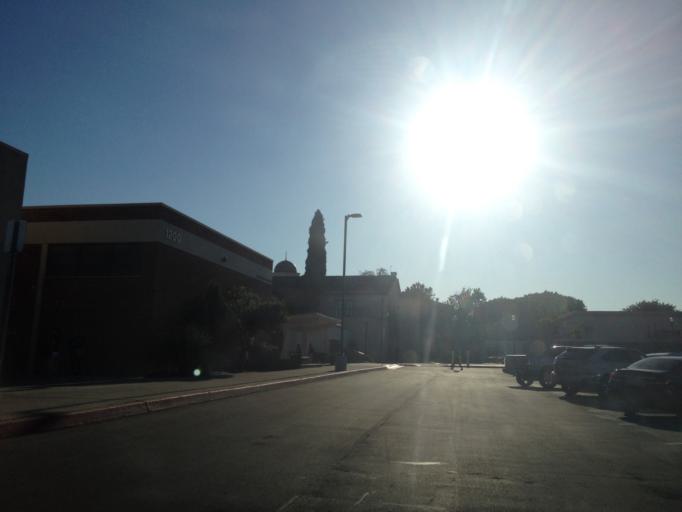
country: US
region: California
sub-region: Orange County
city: Fullerton
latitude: 33.8759
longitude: -117.9166
